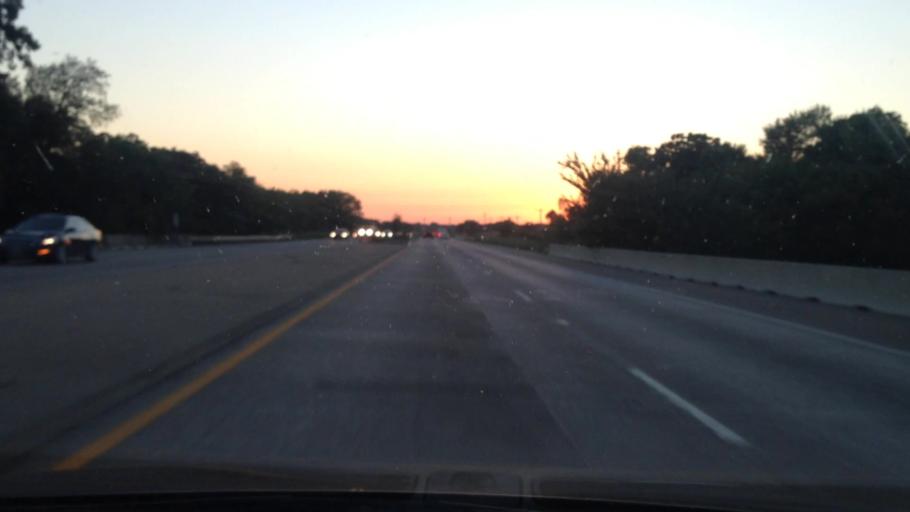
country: US
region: Texas
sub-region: Denton County
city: Lewisville
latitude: 33.0459
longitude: -96.9614
